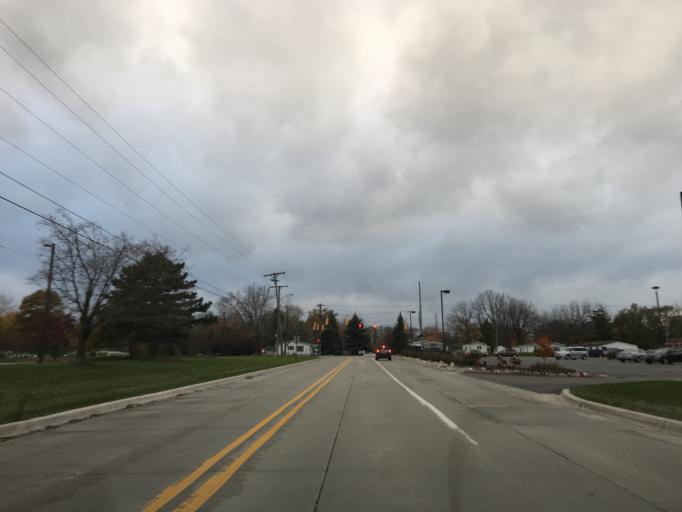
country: US
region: Michigan
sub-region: Oakland County
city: Novi
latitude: 42.4899
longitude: -83.4346
